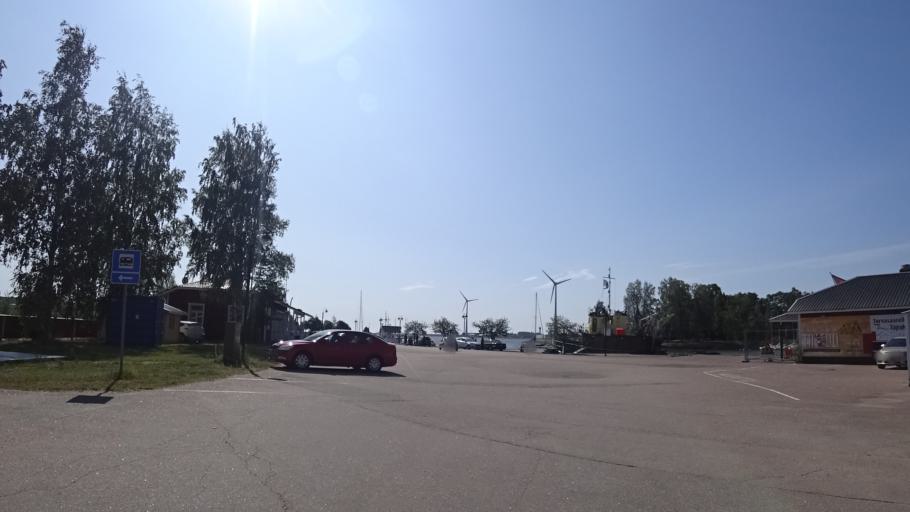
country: FI
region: Kymenlaakso
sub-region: Kotka-Hamina
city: Hamina
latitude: 60.5618
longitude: 27.1819
